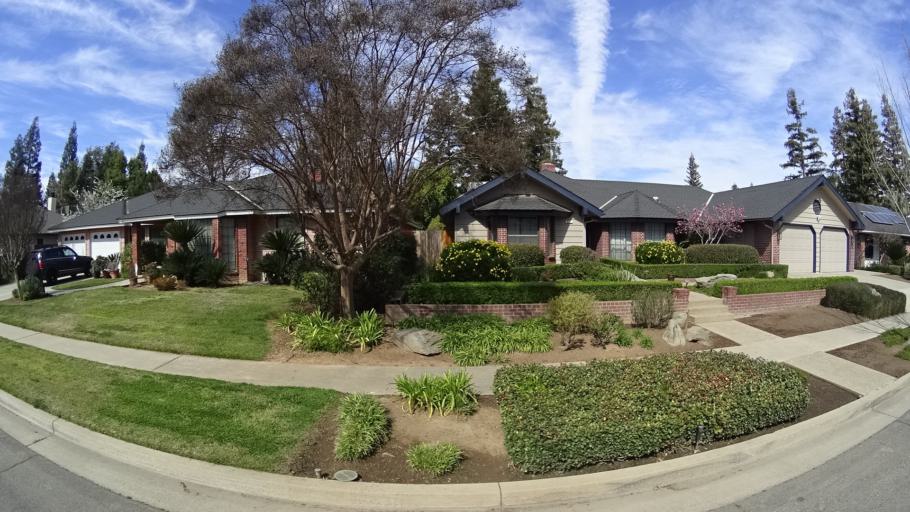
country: US
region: California
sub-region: Fresno County
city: Clovis
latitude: 36.8608
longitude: -119.7713
